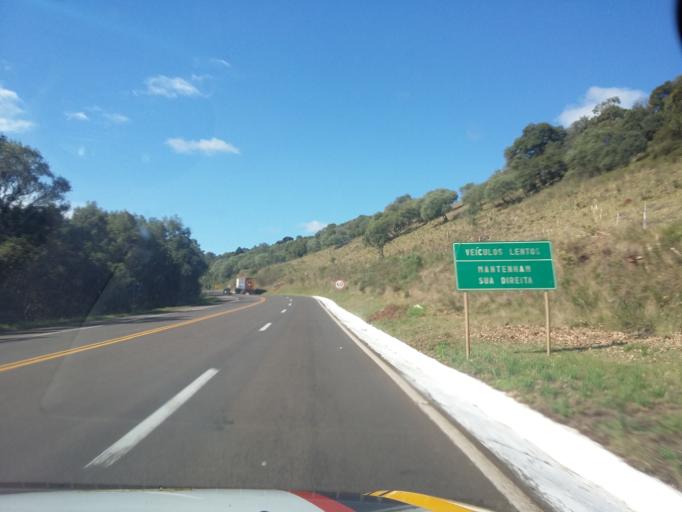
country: BR
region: Rio Grande do Sul
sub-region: Vacaria
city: Vacaria
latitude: -28.5706
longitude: -51.0115
